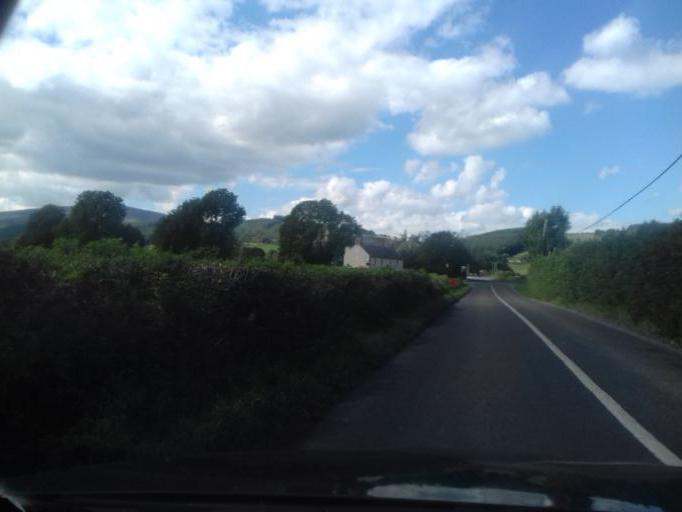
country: IE
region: Munster
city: Carrick-on-Suir
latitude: 52.3929
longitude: -7.4704
